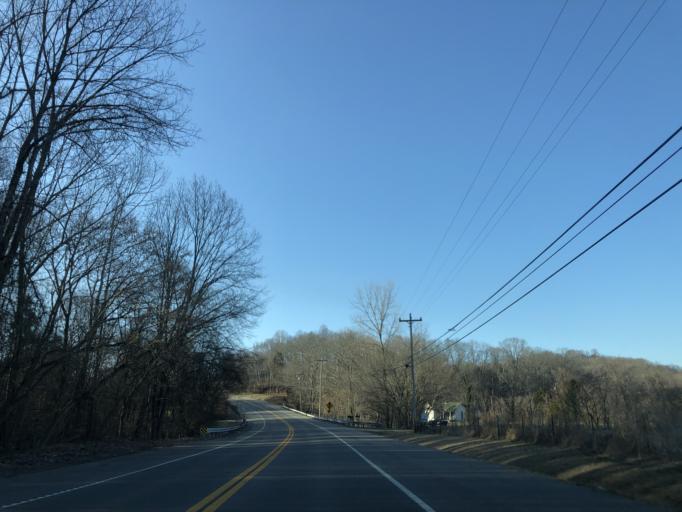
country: US
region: Tennessee
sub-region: Sumner County
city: White House
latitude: 36.4664
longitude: -86.5607
